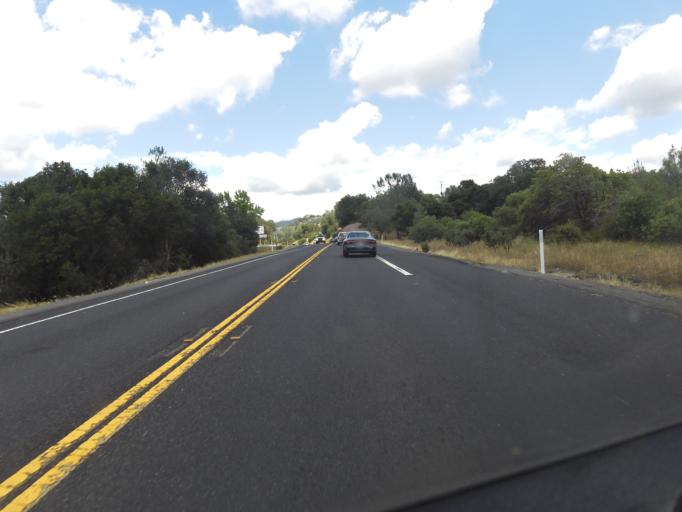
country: US
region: California
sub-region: Madera County
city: Coarsegold
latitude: 37.2434
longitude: -119.7066
